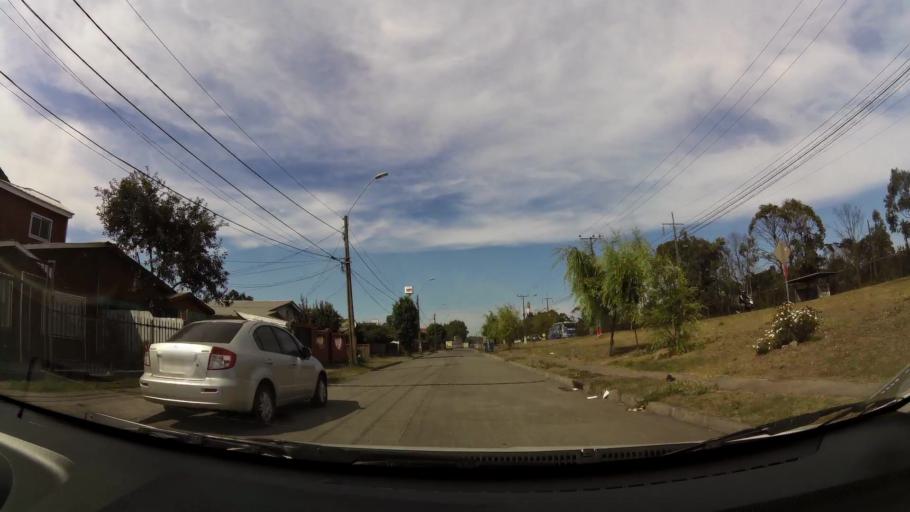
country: CL
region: Biobio
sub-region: Provincia de Concepcion
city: Talcahuano
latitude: -36.7326
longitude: -73.1187
